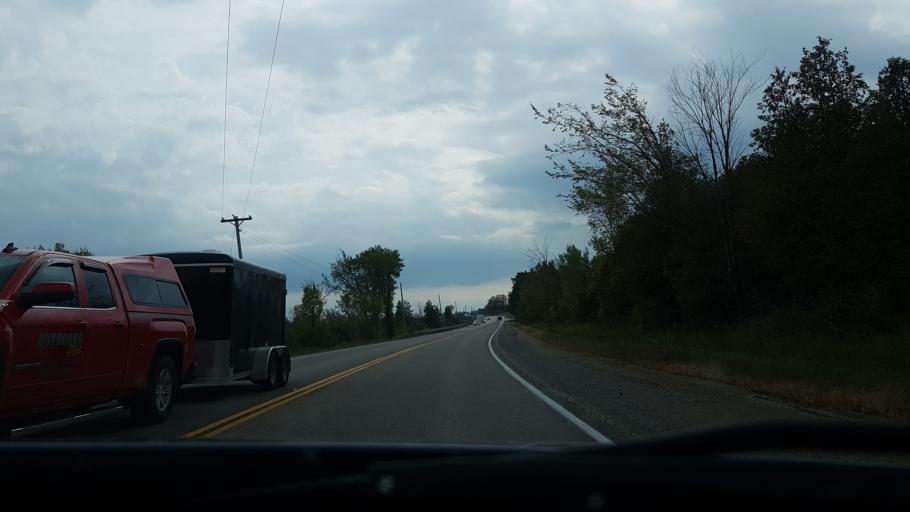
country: CA
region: Ontario
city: Omemee
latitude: 44.4613
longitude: -78.7639
